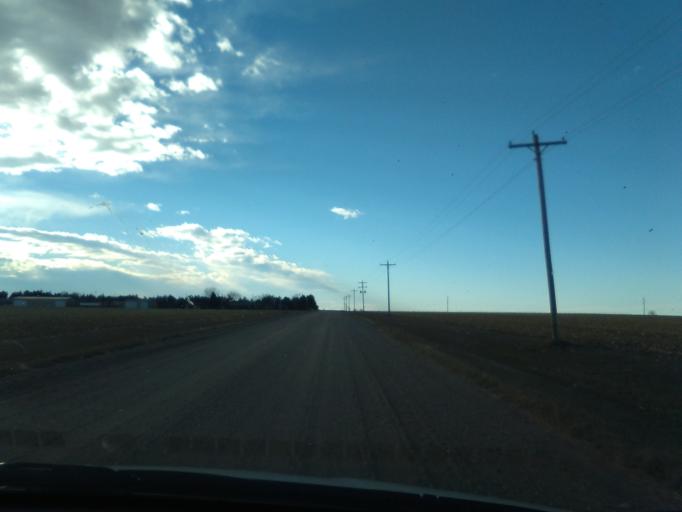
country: US
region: Nebraska
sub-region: Kearney County
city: Minden
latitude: 40.3648
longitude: -98.8595
